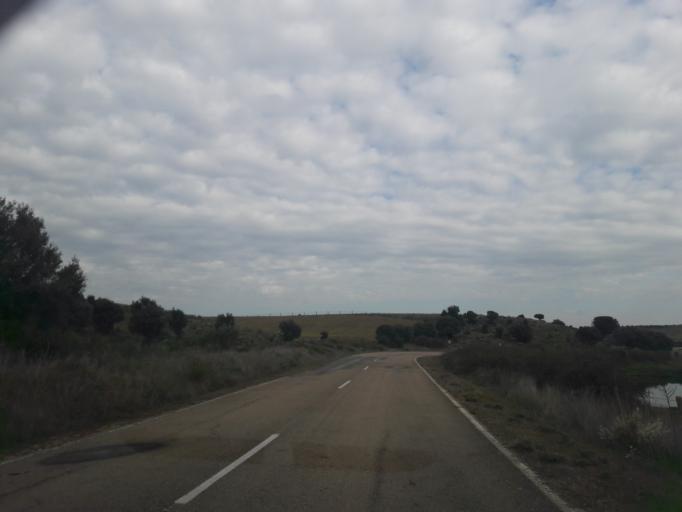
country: ES
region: Castille and Leon
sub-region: Provincia de Salamanca
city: Pastores
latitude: 40.5406
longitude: -6.5276
